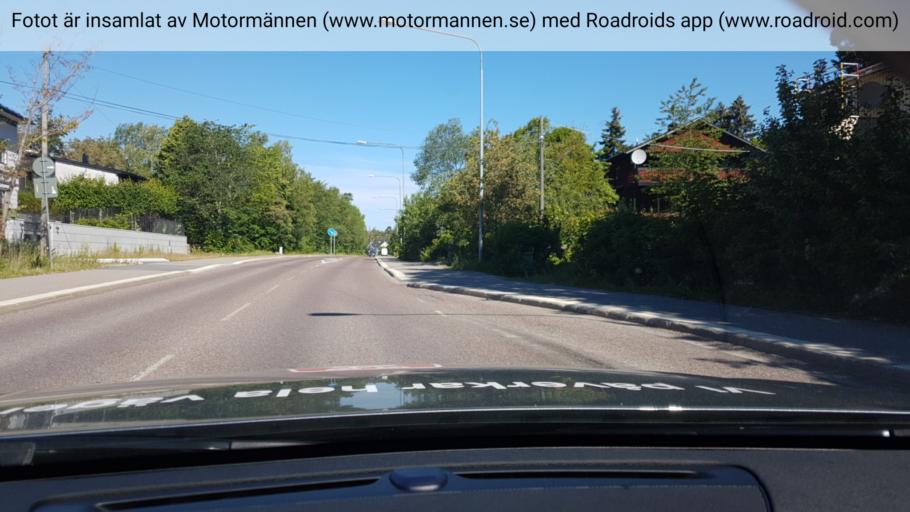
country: SE
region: Stockholm
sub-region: Huddinge Kommun
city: Huddinge
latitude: 59.2561
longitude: 17.9815
